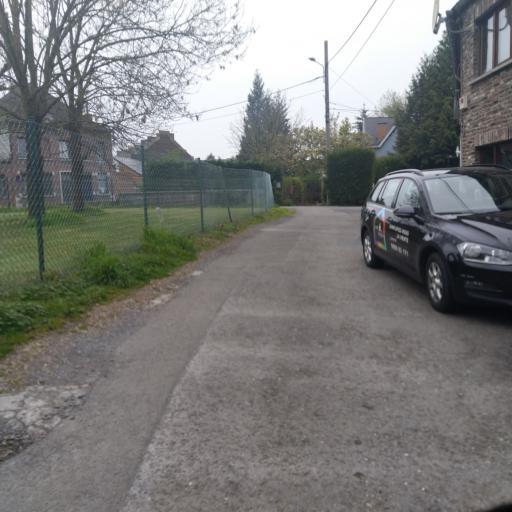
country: BE
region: Wallonia
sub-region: Province du Hainaut
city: Mons
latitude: 50.4777
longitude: 3.9570
